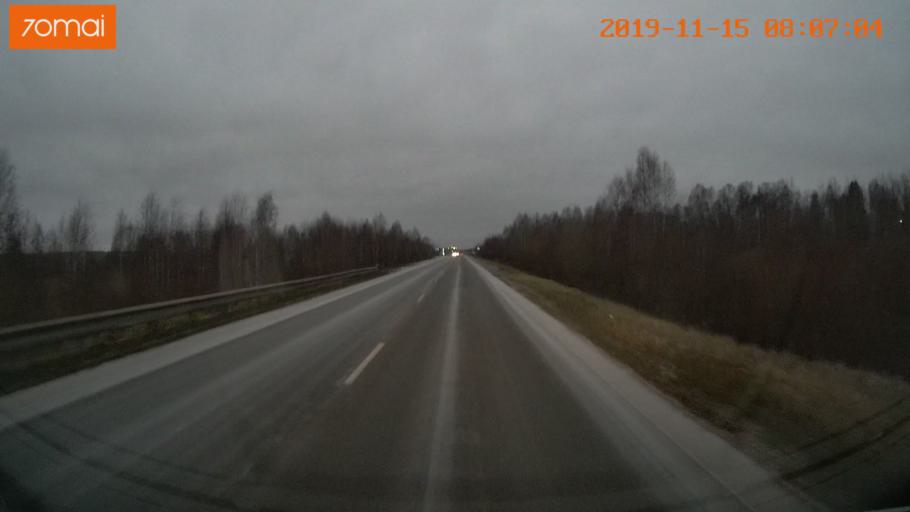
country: RU
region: Vologda
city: Cherepovets
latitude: 59.0249
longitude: 38.0242
